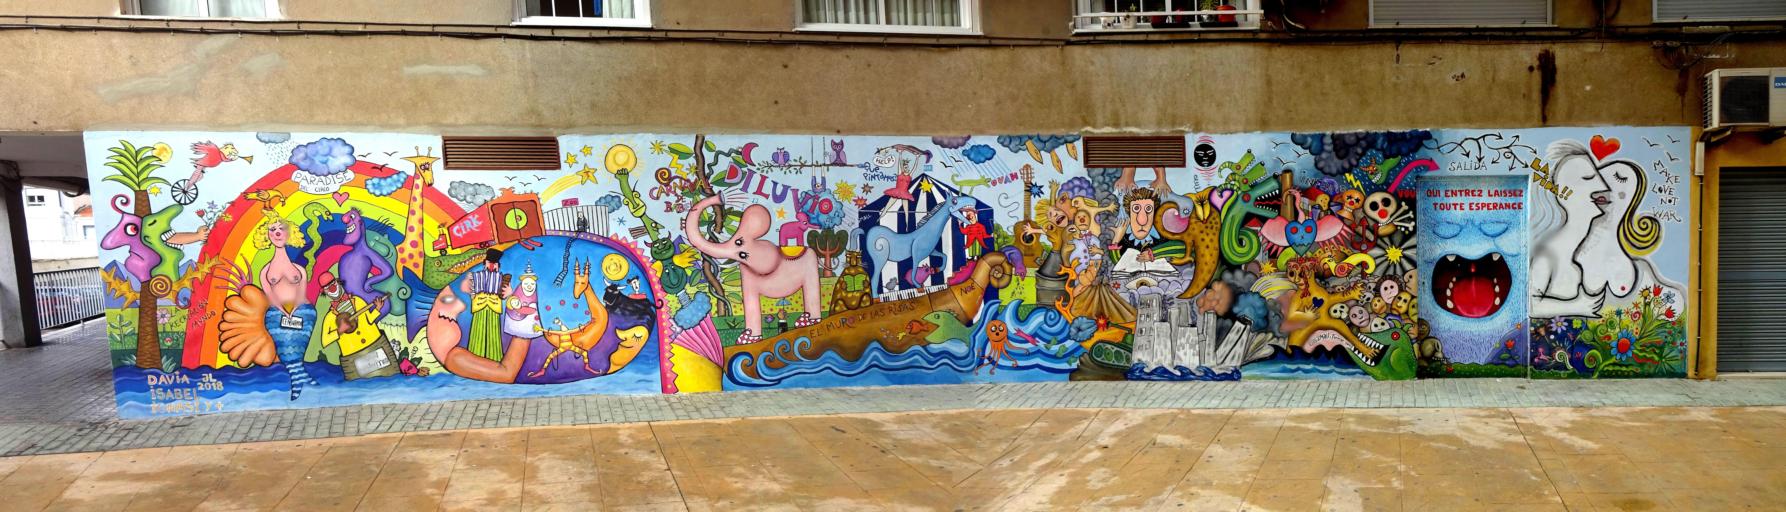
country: ES
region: Valencia
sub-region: Provincia de Alicante
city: Elda
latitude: 38.4852
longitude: -0.7706
